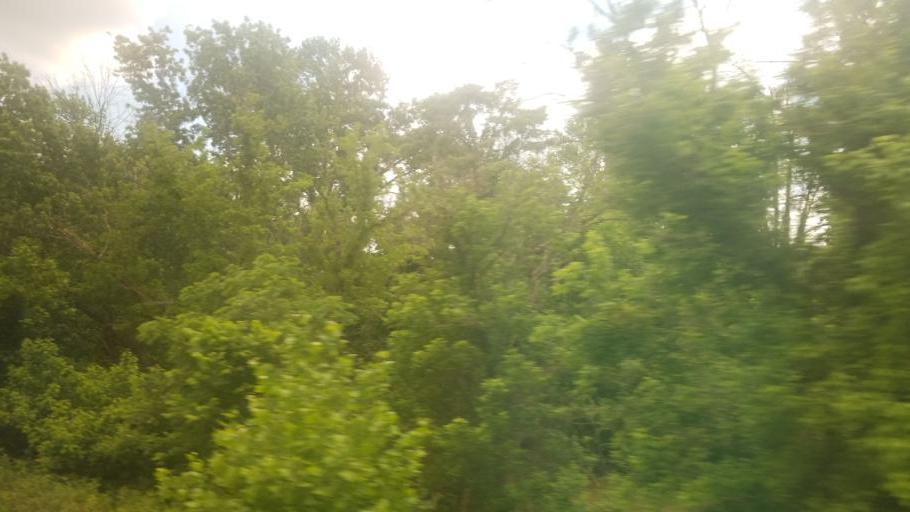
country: US
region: Maryland
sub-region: Frederick County
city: Brunswick
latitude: 39.3079
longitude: -77.6134
